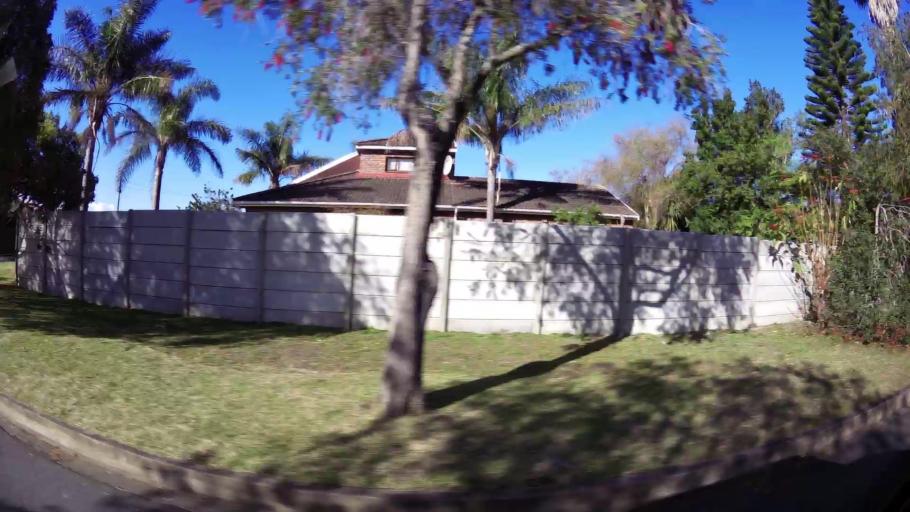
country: ZA
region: Western Cape
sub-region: Eden District Municipality
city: George
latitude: -33.9589
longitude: 22.4219
